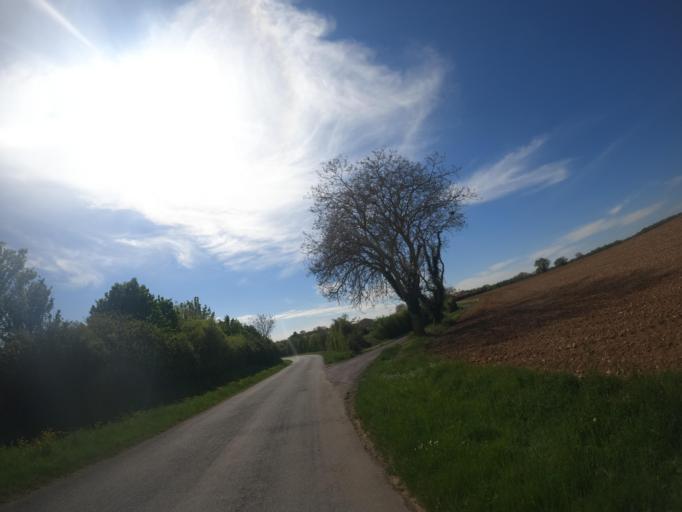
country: FR
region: Poitou-Charentes
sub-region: Departement des Deux-Sevres
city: Airvault
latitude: 46.8860
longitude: -0.1310
